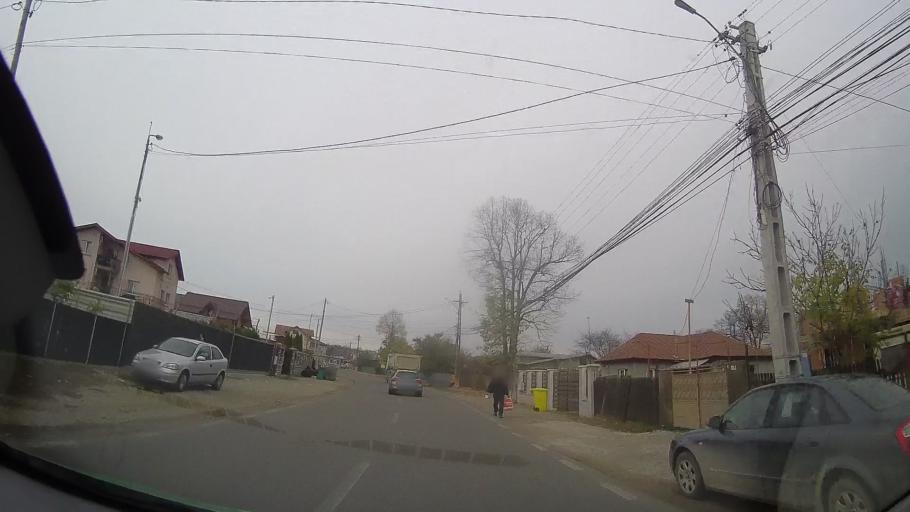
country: RO
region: Prahova
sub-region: Oras Baicoi
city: Liliesti
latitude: 45.0330
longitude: 25.8857
